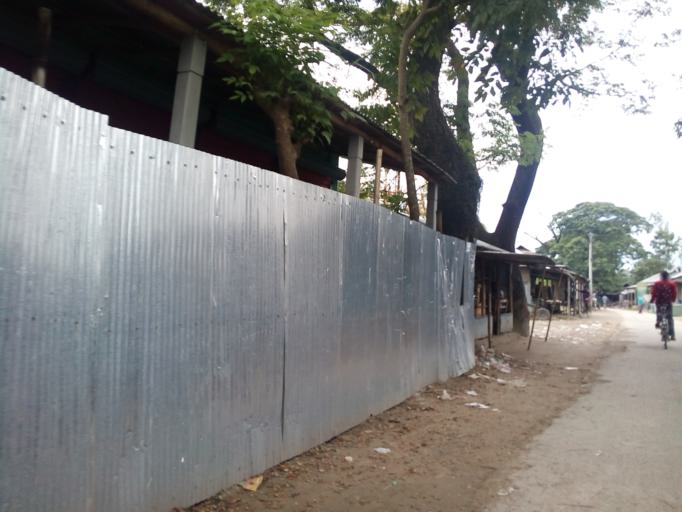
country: BD
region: Rangpur Division
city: Nageswari
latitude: 25.8906
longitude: 89.7111
